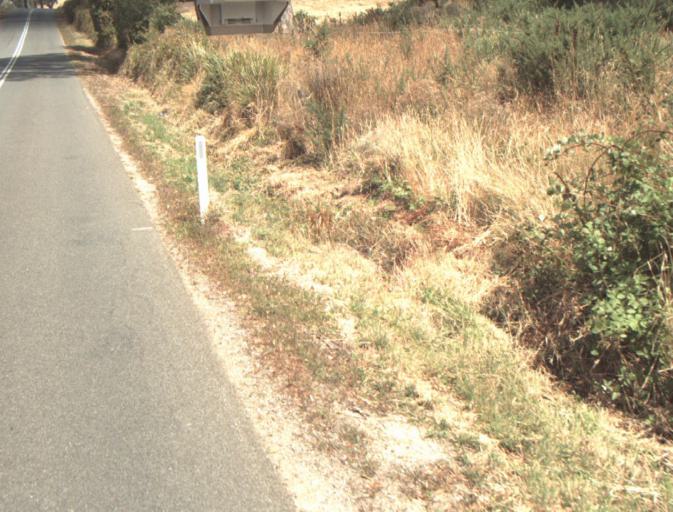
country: AU
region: Tasmania
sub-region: Launceston
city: Mayfield
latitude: -41.2267
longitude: 147.1227
